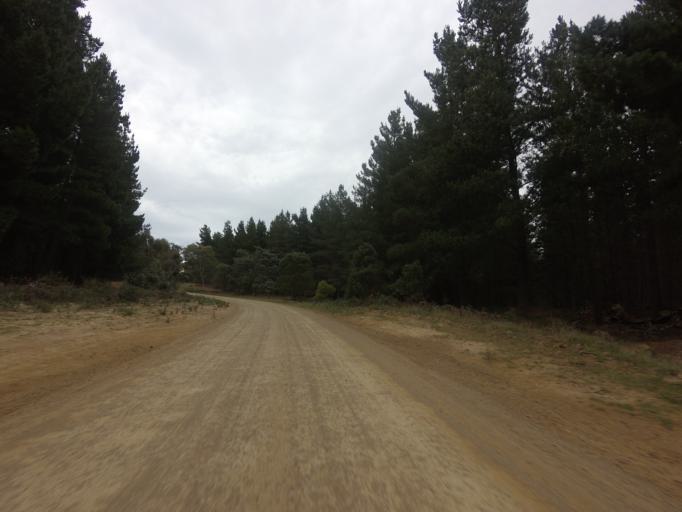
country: AU
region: Tasmania
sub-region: Derwent Valley
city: New Norfolk
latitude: -42.5716
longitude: 146.9951
